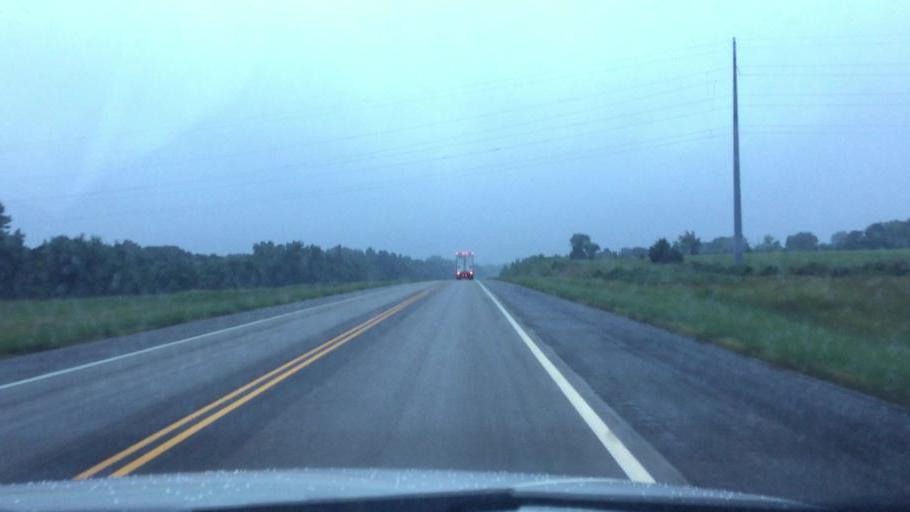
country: US
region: Kansas
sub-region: Montgomery County
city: Cherryvale
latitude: 37.4519
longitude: -95.4830
